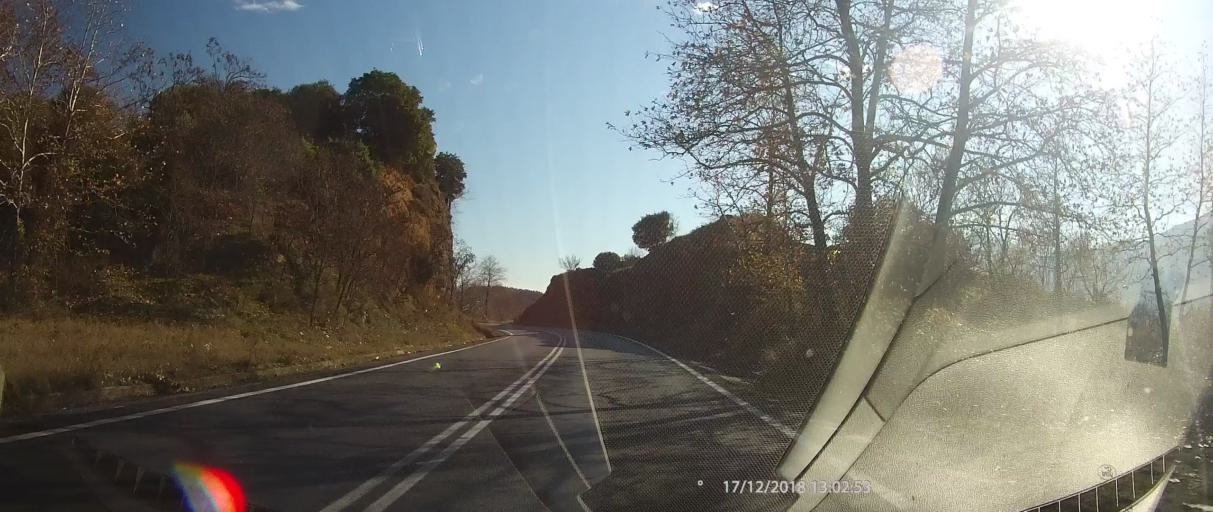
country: GR
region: Thessaly
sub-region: Trikala
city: Kastraki
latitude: 39.7178
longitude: 21.5961
